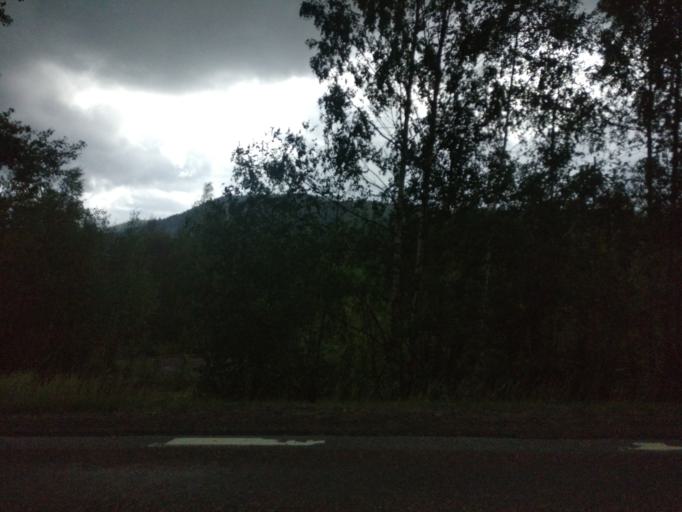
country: SE
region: Vaermland
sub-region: Torsby Kommun
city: Torsby
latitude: 60.7404
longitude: 12.8426
